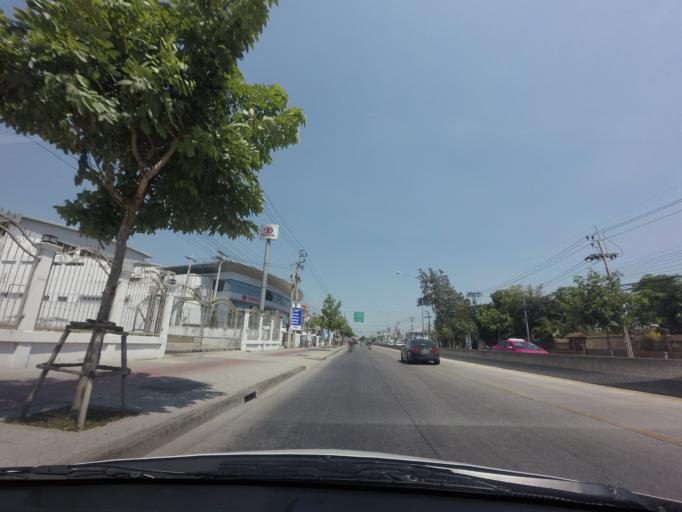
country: TH
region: Bangkok
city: Nong Chok
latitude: 13.8558
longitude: 100.8530
